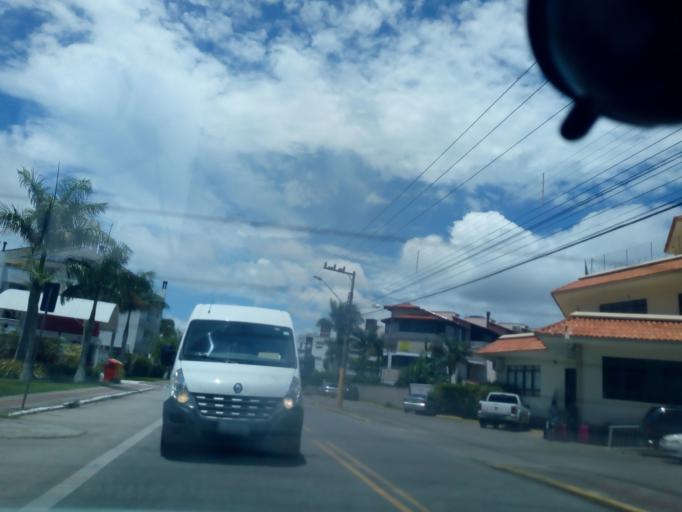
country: BR
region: Santa Catarina
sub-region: Florianopolis
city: Itacorubi
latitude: -27.4101
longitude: -48.4244
